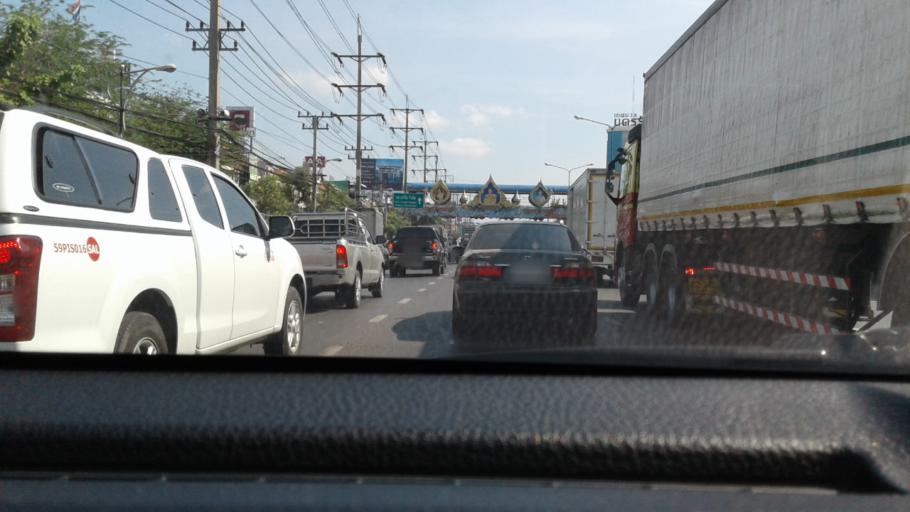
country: TH
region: Phra Nakhon Si Ayutthaya
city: Ban Bang Kadi Pathum Thani
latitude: 13.9869
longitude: 100.6064
